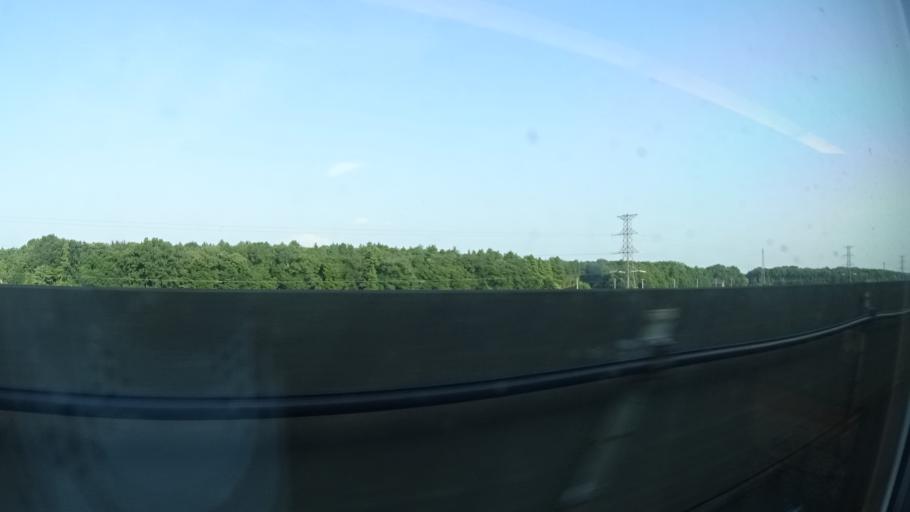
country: JP
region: Ibaraki
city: Koga
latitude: 36.2357
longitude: 139.7611
